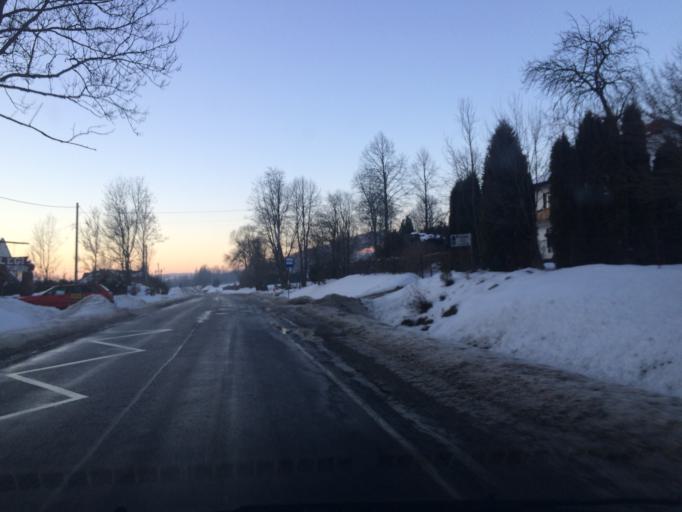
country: PL
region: Subcarpathian Voivodeship
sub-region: Powiat bieszczadzki
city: Czarna
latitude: 49.3590
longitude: 22.6731
